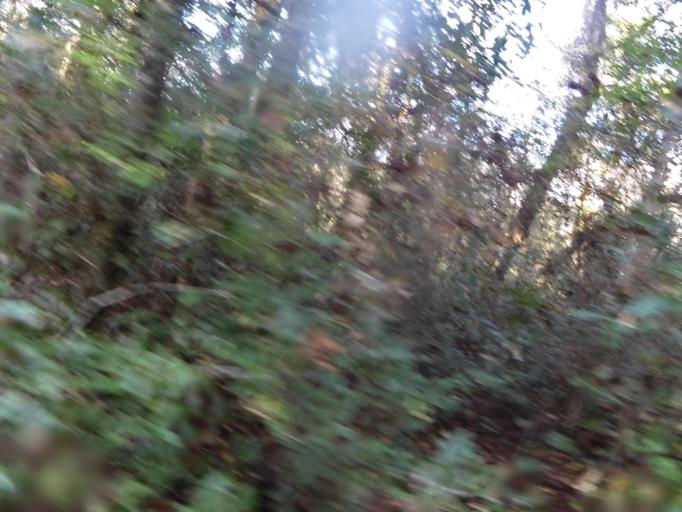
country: US
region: Florida
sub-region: Clay County
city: Middleburg
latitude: 30.1411
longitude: -81.9338
